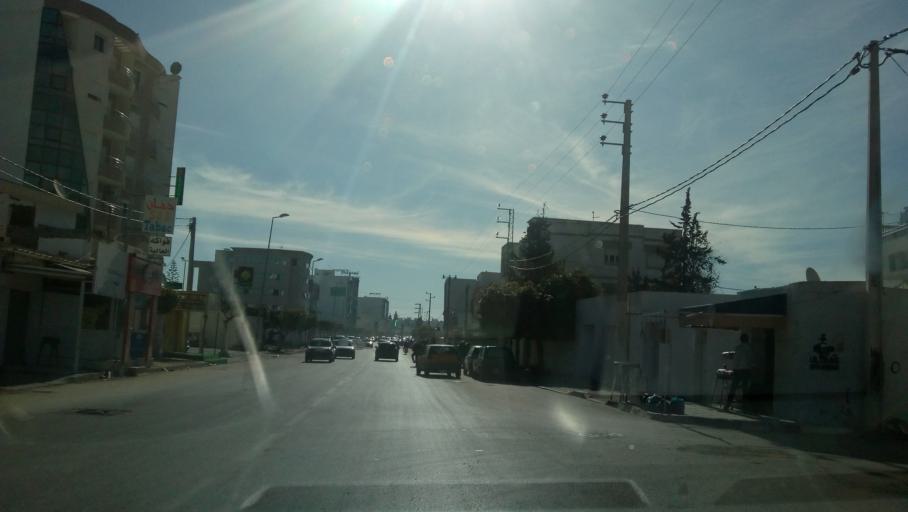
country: TN
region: Safaqis
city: Sfax
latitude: 34.7490
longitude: 10.7348
